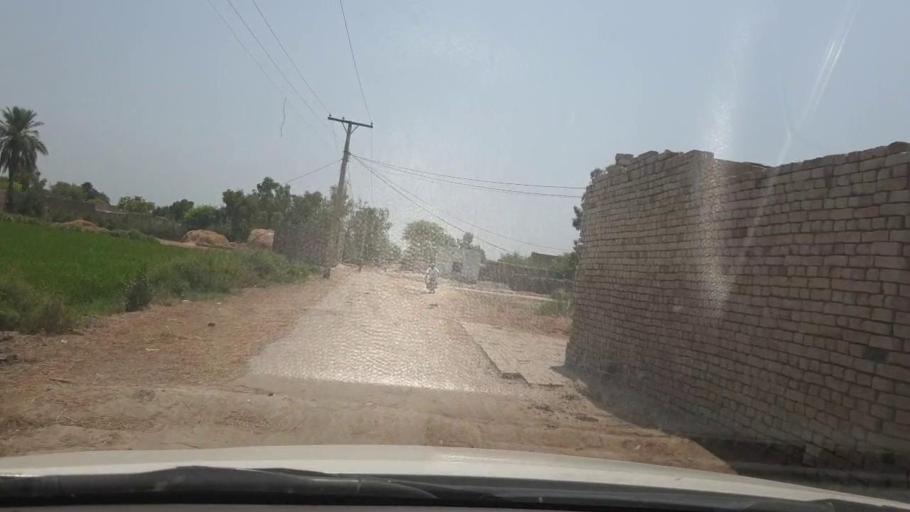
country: PK
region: Sindh
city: Shikarpur
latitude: 28.0686
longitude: 68.5366
